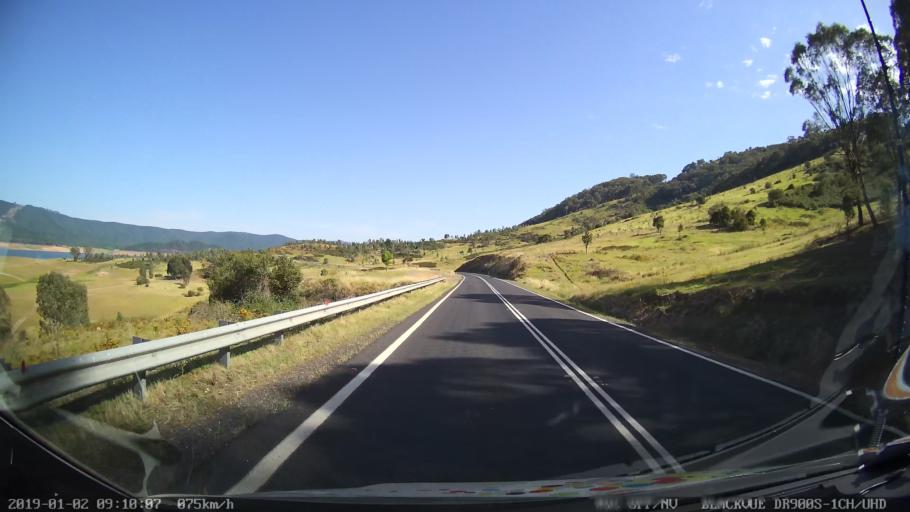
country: AU
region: New South Wales
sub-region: Tumut Shire
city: Tumut
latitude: -35.5246
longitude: 148.2721
